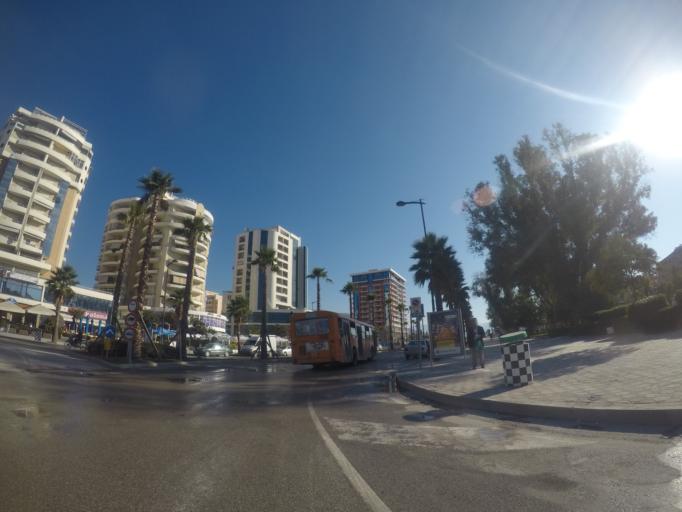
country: AL
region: Vlore
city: Vlore
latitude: 40.4544
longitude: 19.4863
